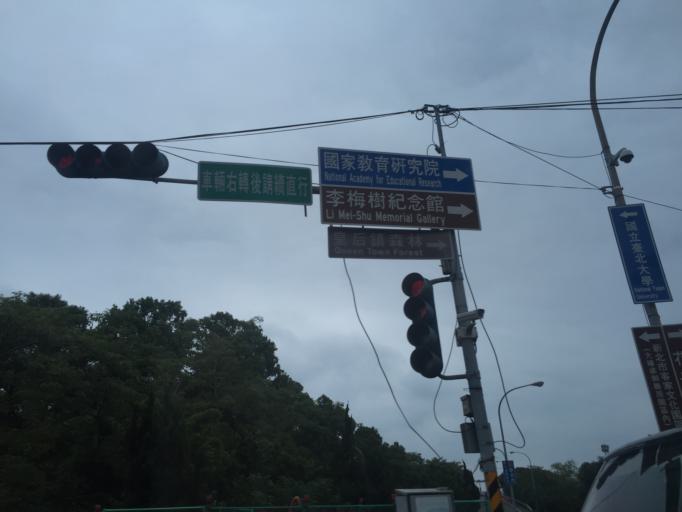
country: TW
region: Taiwan
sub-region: Taoyuan
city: Taoyuan
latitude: 24.9386
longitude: 121.3609
